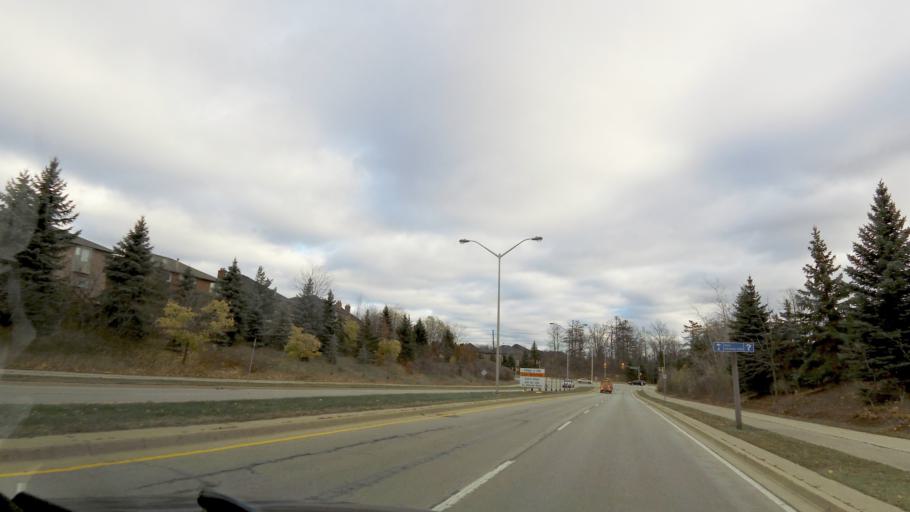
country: CA
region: Ontario
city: Oakville
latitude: 43.4610
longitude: -79.7217
